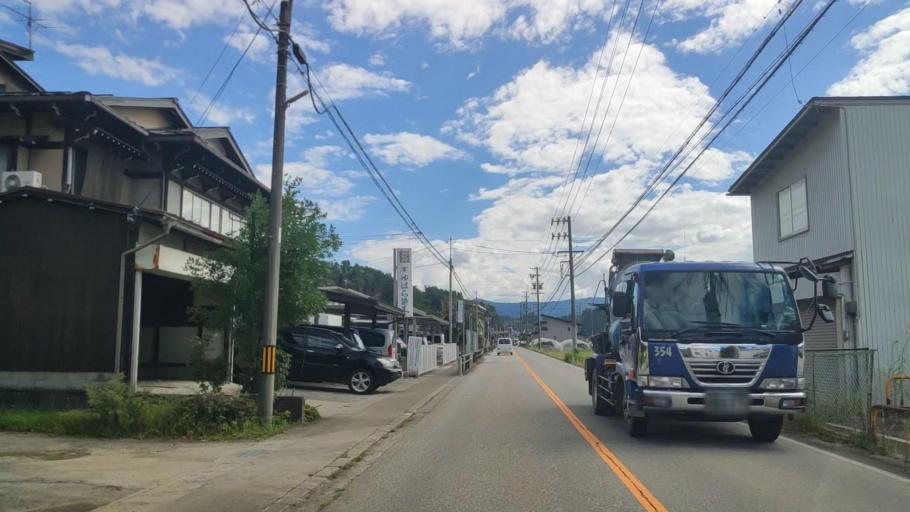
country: JP
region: Gifu
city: Takayama
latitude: 36.1642
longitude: 137.2508
